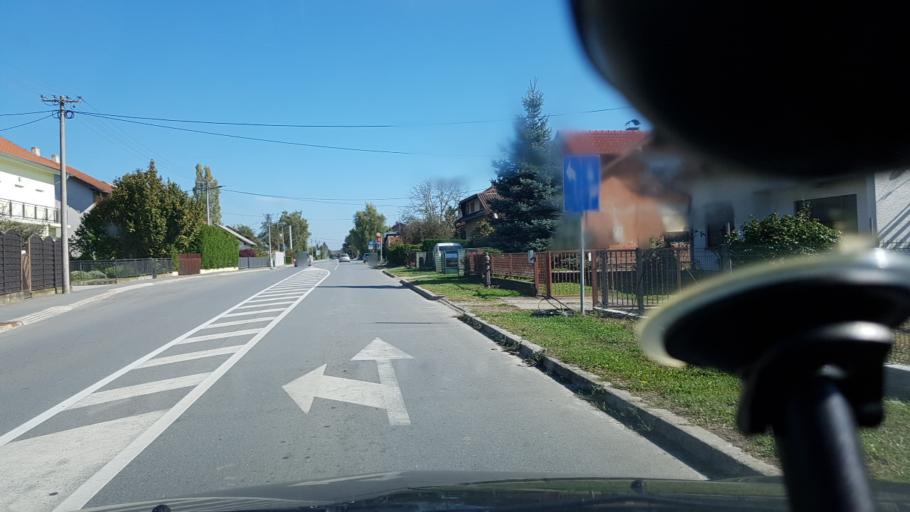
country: HR
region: Zagrebacka
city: Lupoglav
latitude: 45.6958
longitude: 16.3771
